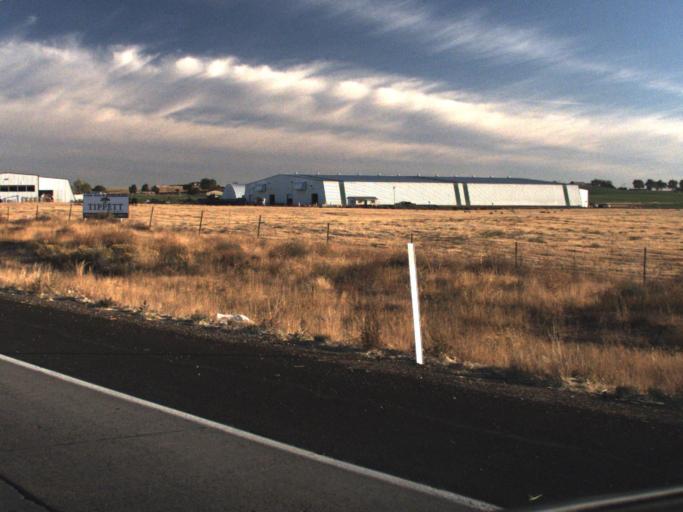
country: US
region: Washington
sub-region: Franklin County
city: Pasco
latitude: 46.2728
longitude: -119.0892
